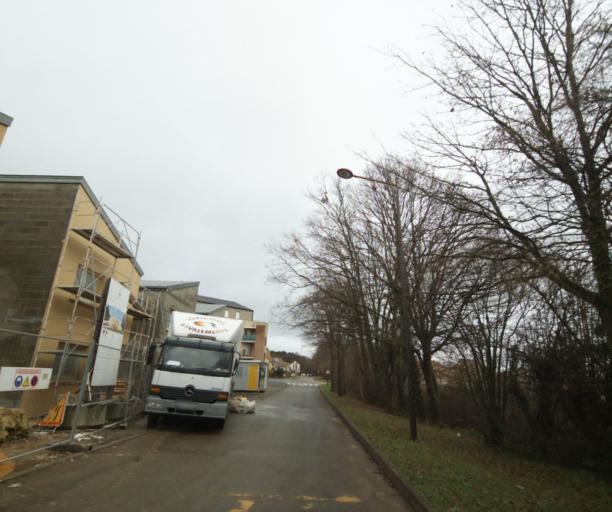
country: FR
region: Pays de la Loire
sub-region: Departement de la Sarthe
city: Rouillon
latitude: 48.0191
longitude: 0.1468
